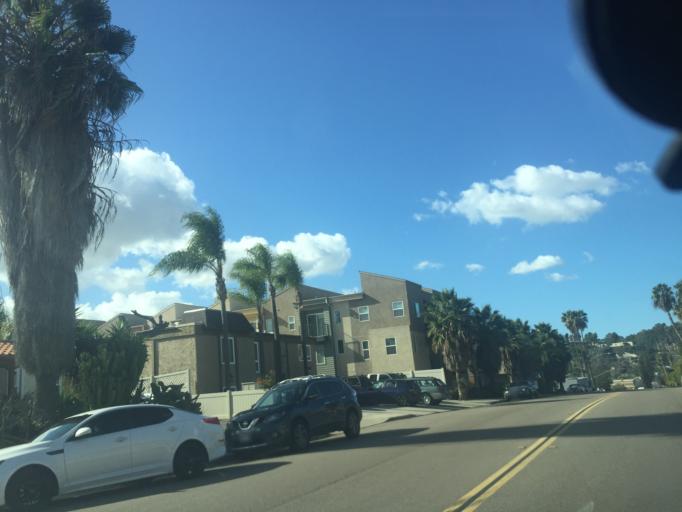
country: US
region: California
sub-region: San Diego County
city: La Mesa
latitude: 32.7899
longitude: -117.0958
